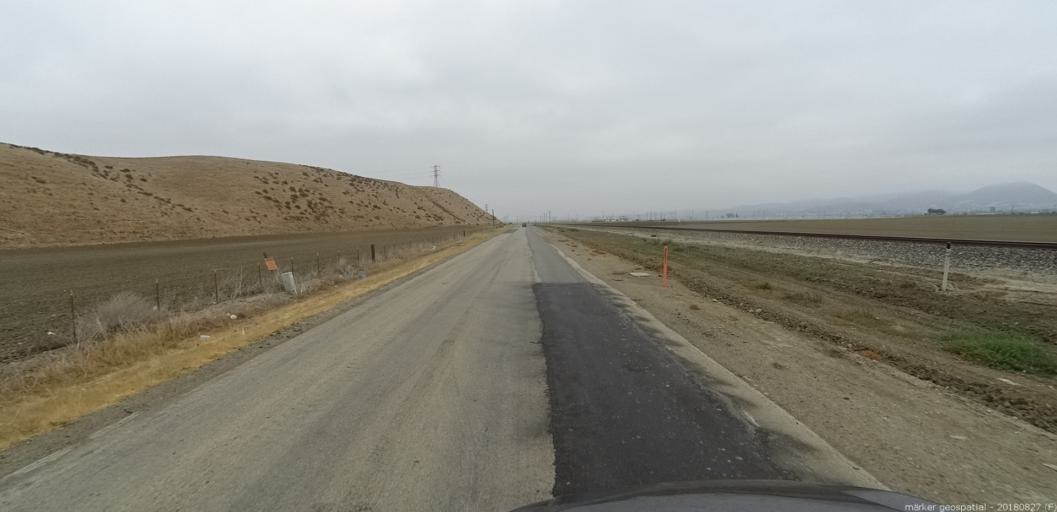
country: US
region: California
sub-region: Monterey County
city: King City
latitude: 36.2741
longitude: -121.1471
